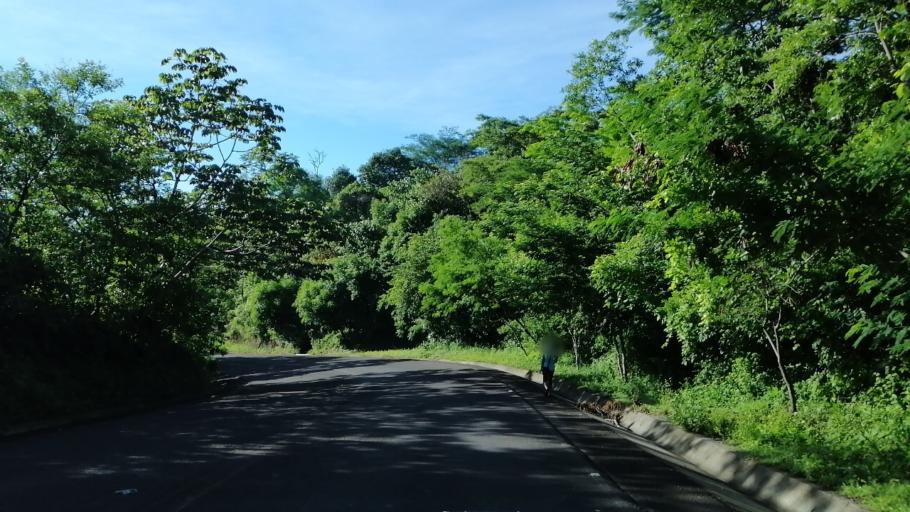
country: SV
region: Morazan
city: Cacaopera
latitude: 13.7906
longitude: -88.1299
